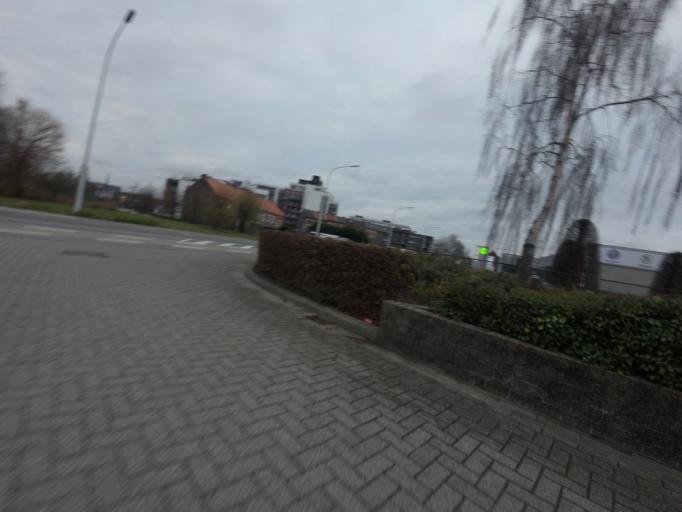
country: BE
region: Flanders
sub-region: Provincie Antwerpen
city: Lier
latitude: 51.1245
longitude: 4.5789
